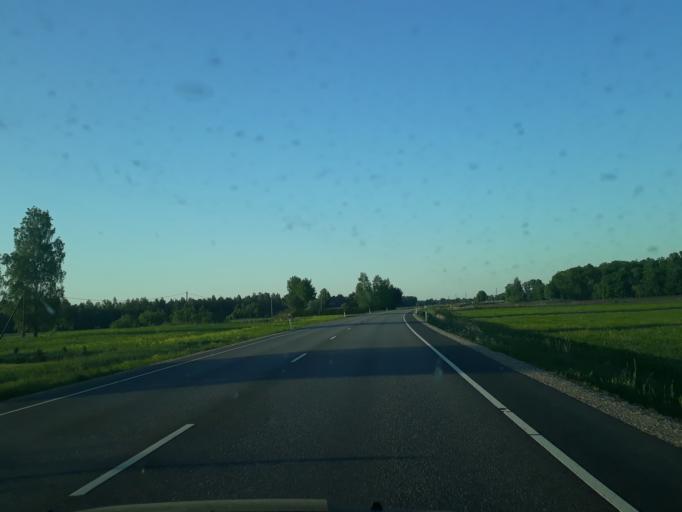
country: EE
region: Paernumaa
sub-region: Tootsi vald
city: Tootsi
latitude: 58.5702
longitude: 24.8760
